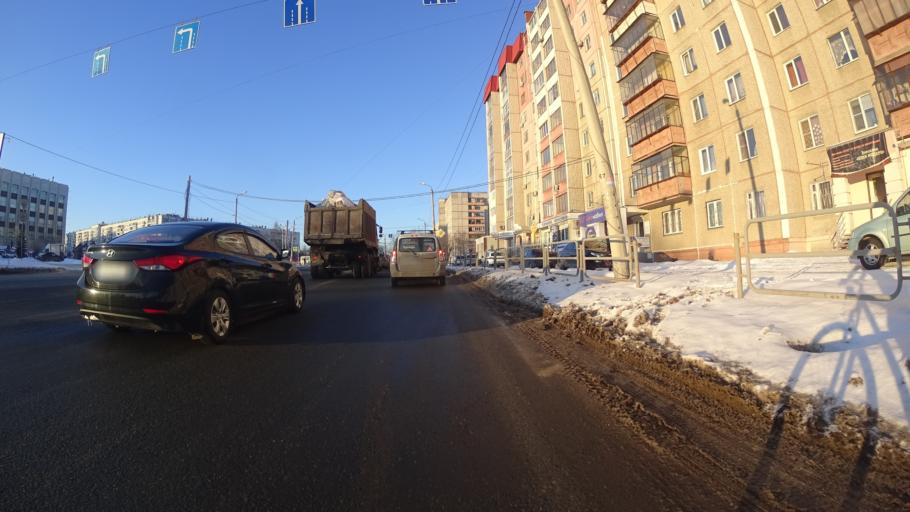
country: RU
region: Chelyabinsk
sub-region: Gorod Chelyabinsk
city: Chelyabinsk
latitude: 55.1907
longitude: 61.3636
